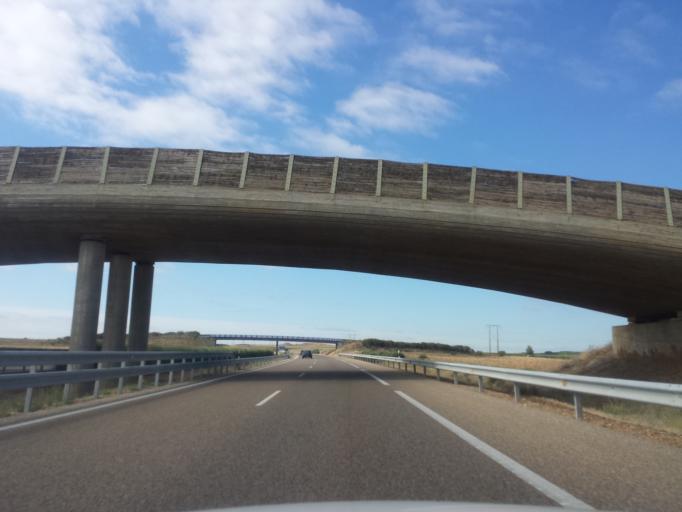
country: ES
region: Castille and Leon
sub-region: Provincia de Leon
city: Villademor de la Vega
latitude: 42.2609
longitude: -5.5939
